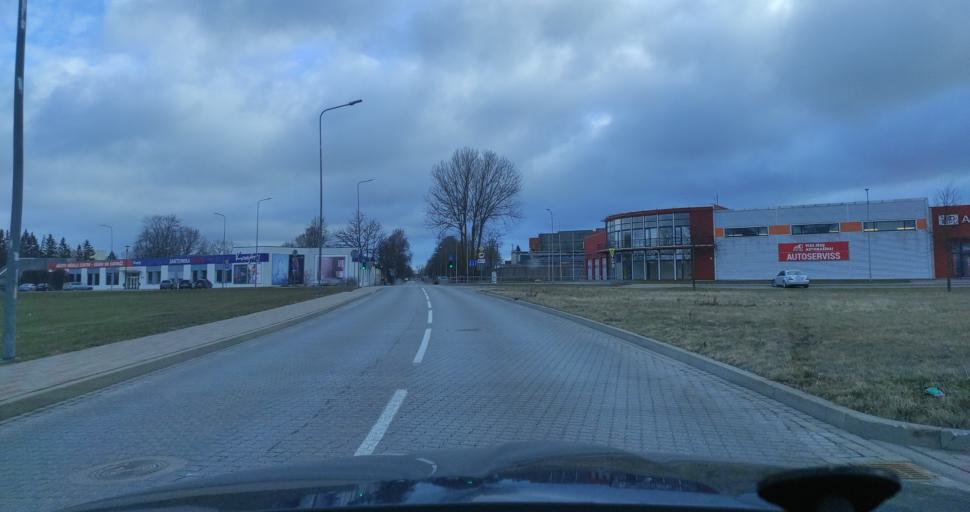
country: LV
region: Ventspils
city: Ventspils
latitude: 57.3833
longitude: 21.5757
